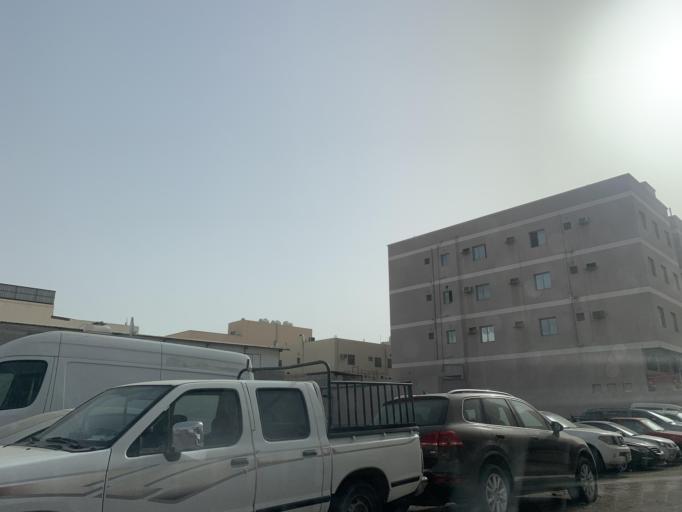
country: BH
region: Northern
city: Madinat `Isa
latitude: 26.1771
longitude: 50.5288
